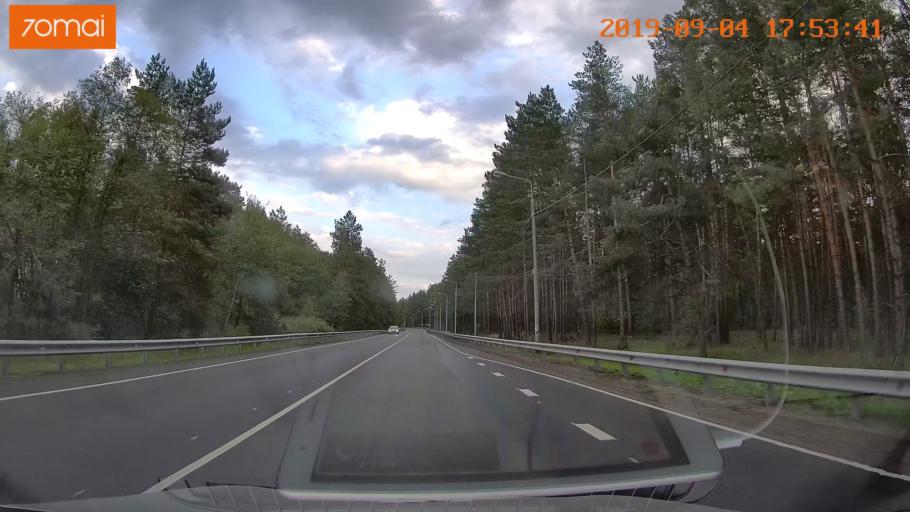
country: RU
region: Moskovskaya
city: Imeni Tsyurupy
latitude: 55.5150
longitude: 38.7265
